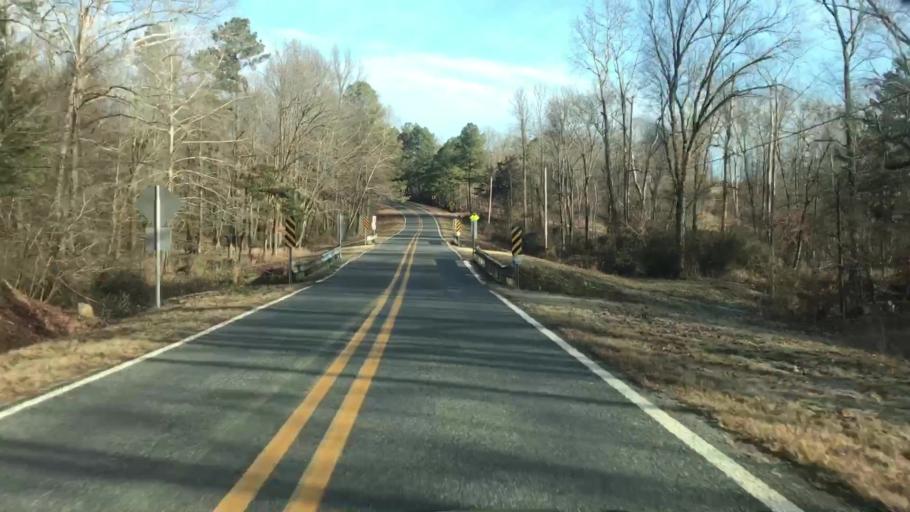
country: US
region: Arkansas
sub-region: Garland County
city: Rockwell
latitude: 34.4907
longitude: -93.2759
